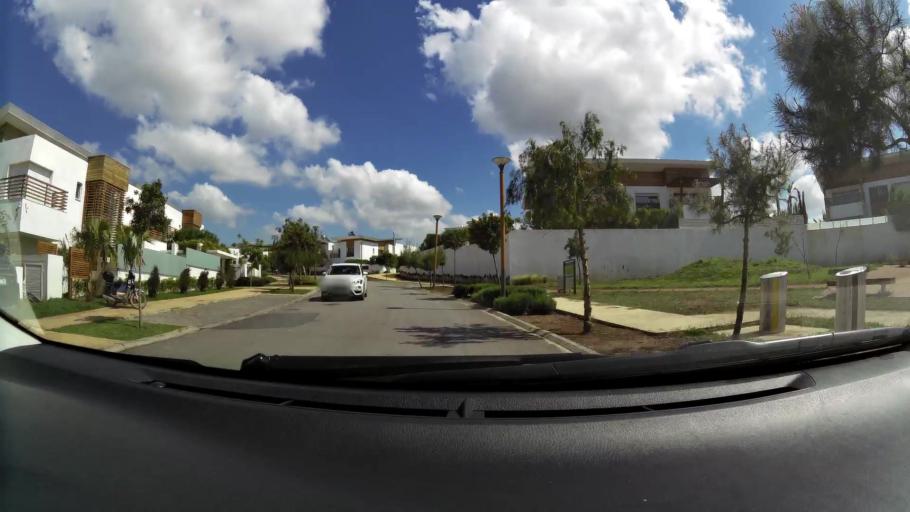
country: MA
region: Grand Casablanca
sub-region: Nouaceur
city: Bouskoura
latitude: 33.4876
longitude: -7.5990
